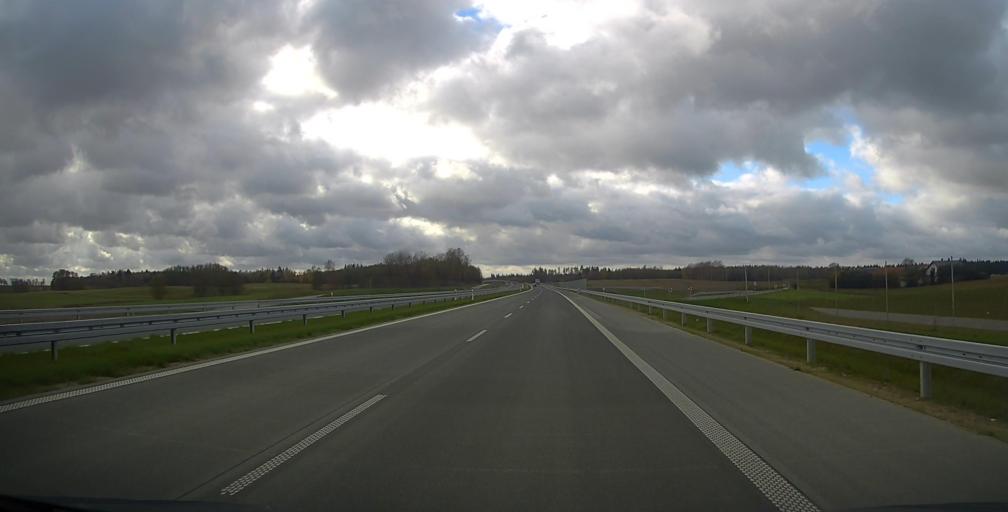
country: PL
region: Podlasie
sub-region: Powiat suwalski
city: Raczki
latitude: 53.9073
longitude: 22.7091
